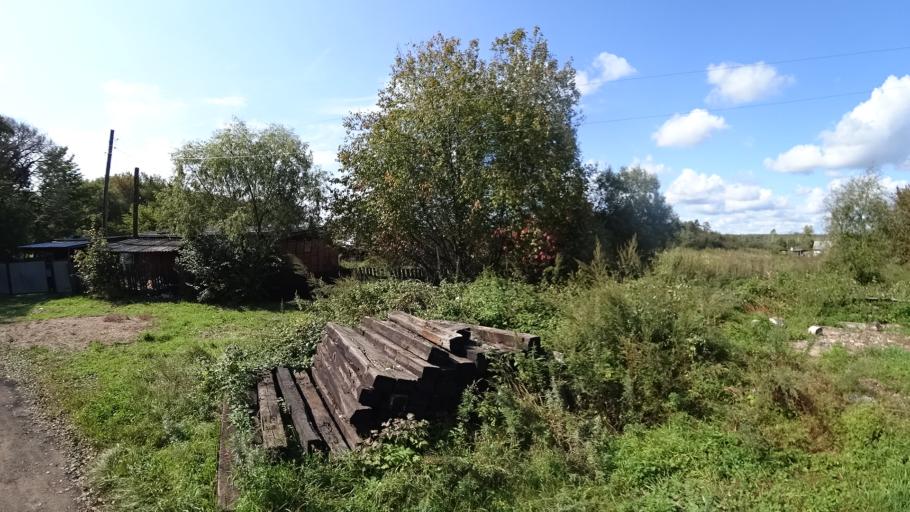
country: RU
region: Amur
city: Arkhara
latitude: 49.4002
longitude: 130.1478
